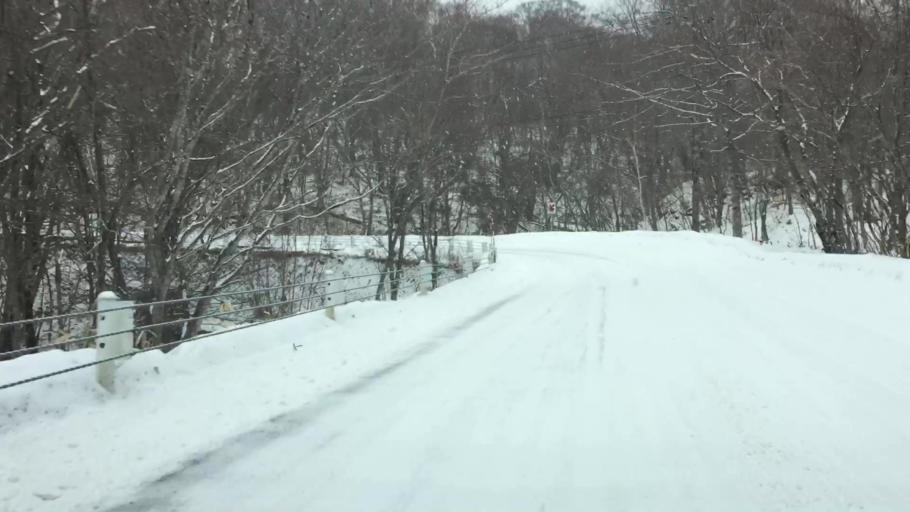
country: JP
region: Tochigi
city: Imaichi
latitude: 36.8973
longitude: 139.7395
